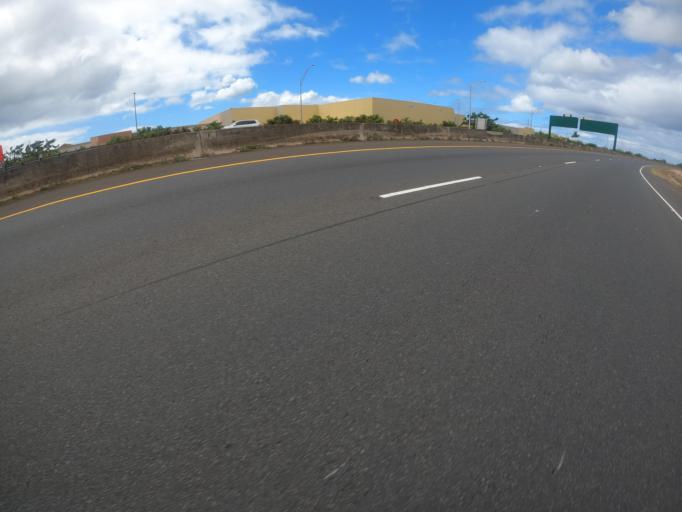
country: US
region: Hawaii
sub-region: Honolulu County
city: Makakilo City
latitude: 21.3318
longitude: -158.0905
